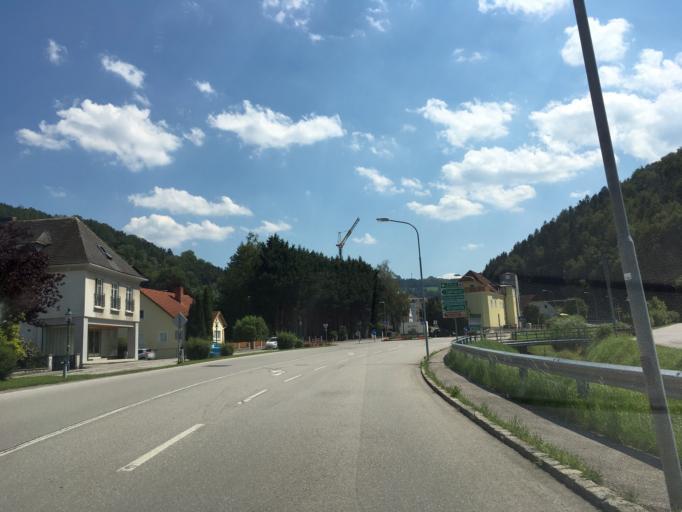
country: AT
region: Lower Austria
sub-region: Politischer Bezirk Neunkirchen
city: Edlitz
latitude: 47.5993
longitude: 16.1387
